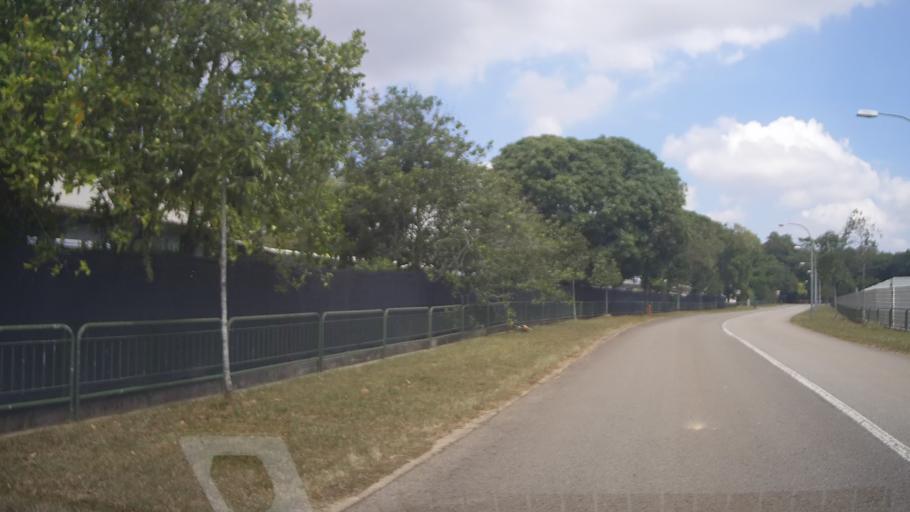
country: MY
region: Johor
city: Johor Bahru
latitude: 1.4429
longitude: 103.7290
